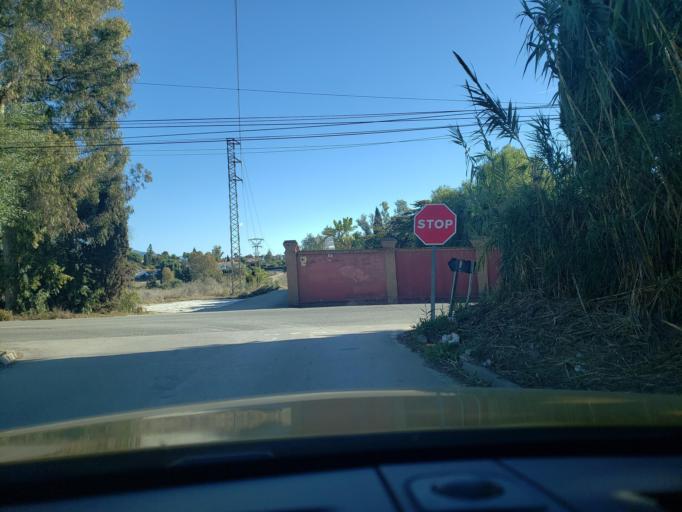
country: ES
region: Andalusia
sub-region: Provincia de Malaga
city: Benahavis
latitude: 36.4853
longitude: -5.0159
